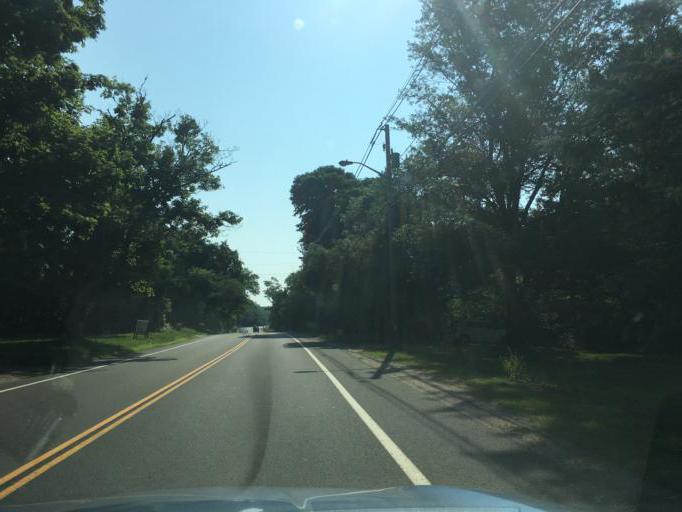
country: US
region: Rhode Island
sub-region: Washington County
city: Kingston
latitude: 41.4909
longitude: -71.4867
